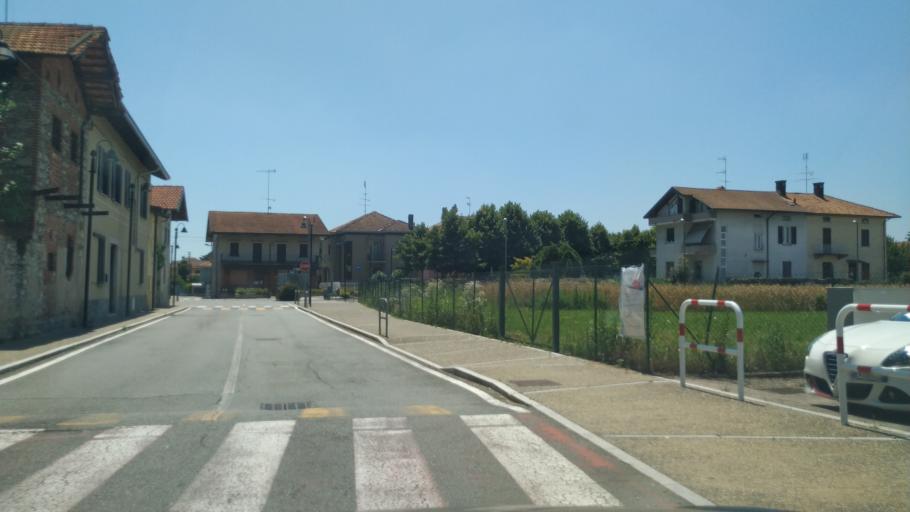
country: IT
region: Piedmont
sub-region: Provincia di Novara
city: Cureggio
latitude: 45.6752
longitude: 8.4596
